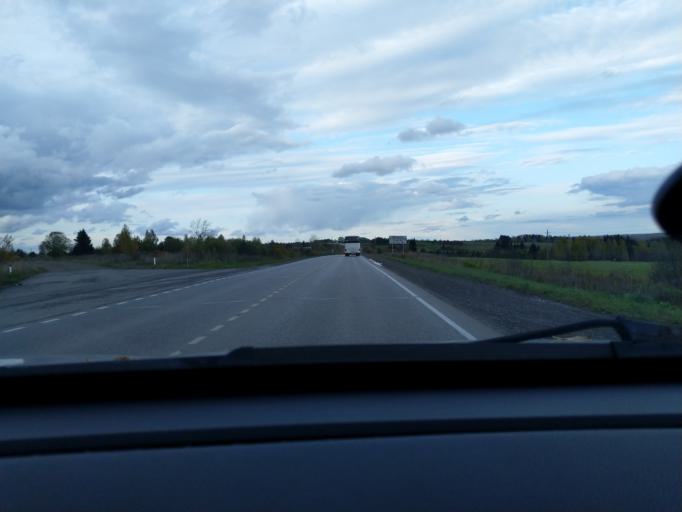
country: RU
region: Perm
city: Polazna
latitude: 58.3522
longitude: 56.4729
